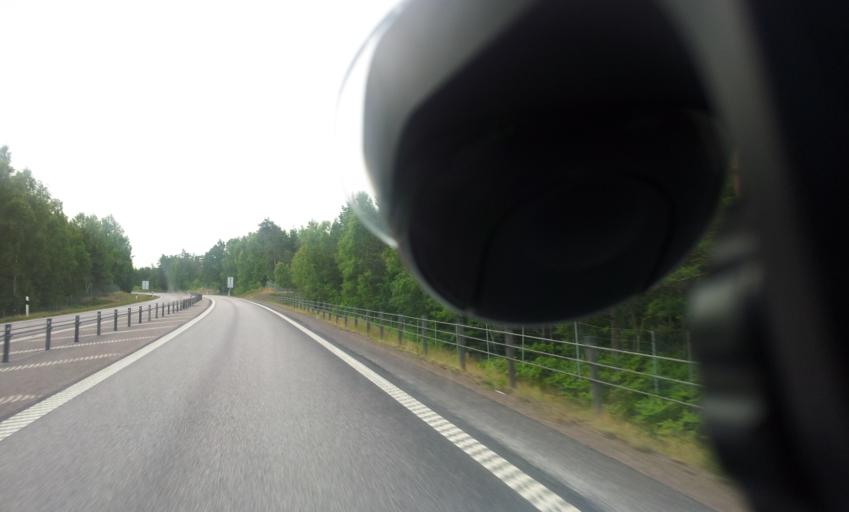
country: SE
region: Kalmar
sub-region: Oskarshamns Kommun
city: Paskallavik
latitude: 57.1637
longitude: 16.4448
